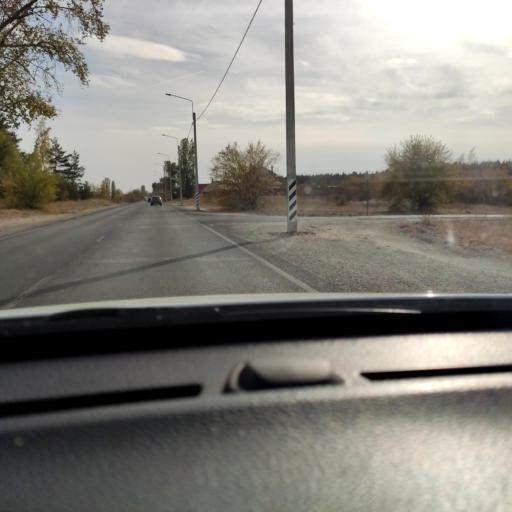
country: RU
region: Voronezj
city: Maslovka
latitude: 51.5770
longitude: 39.2469
